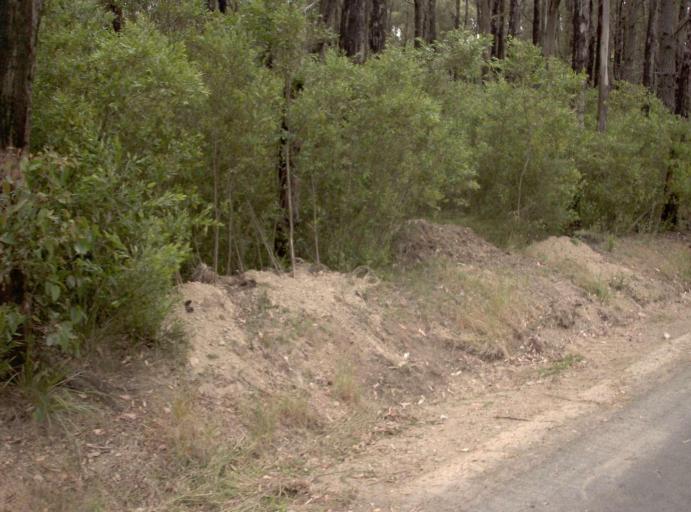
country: AU
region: Victoria
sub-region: Latrobe
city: Moe
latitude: -38.3121
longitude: 146.2677
